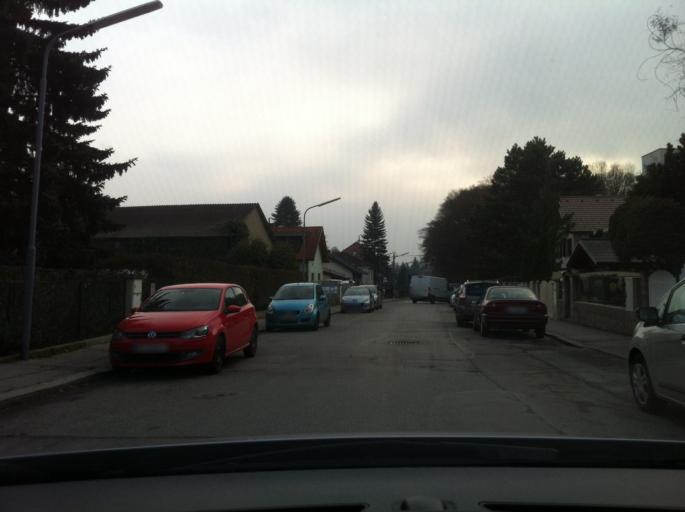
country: AT
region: Lower Austria
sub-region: Politischer Bezirk Wien-Umgebung
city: Purkersdorf
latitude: 48.2227
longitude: 16.2471
